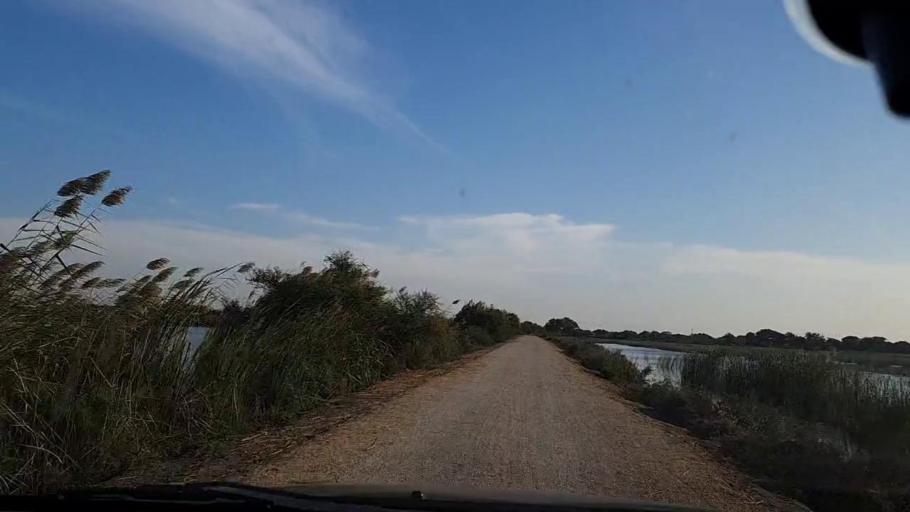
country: PK
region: Sindh
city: Mirpur Batoro
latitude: 24.6540
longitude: 68.2931
